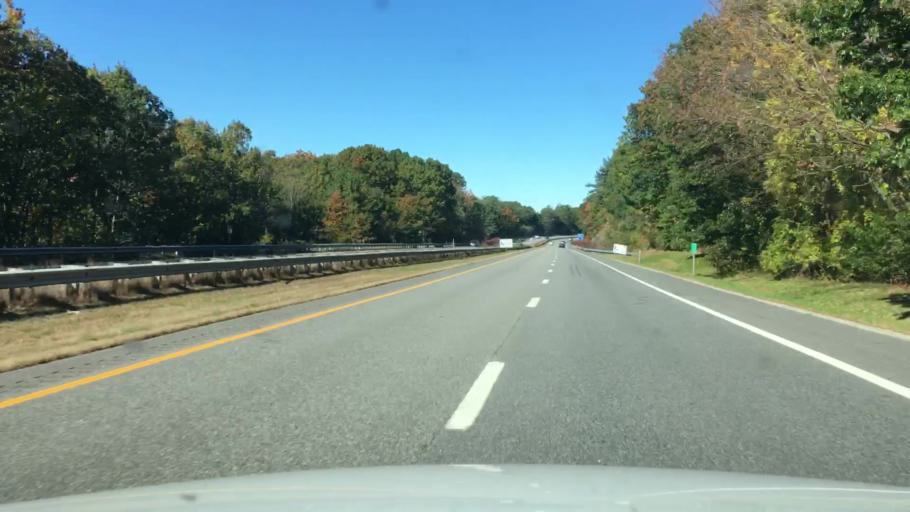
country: US
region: New Hampshire
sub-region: Strafford County
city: Dover
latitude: 43.1733
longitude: -70.8648
